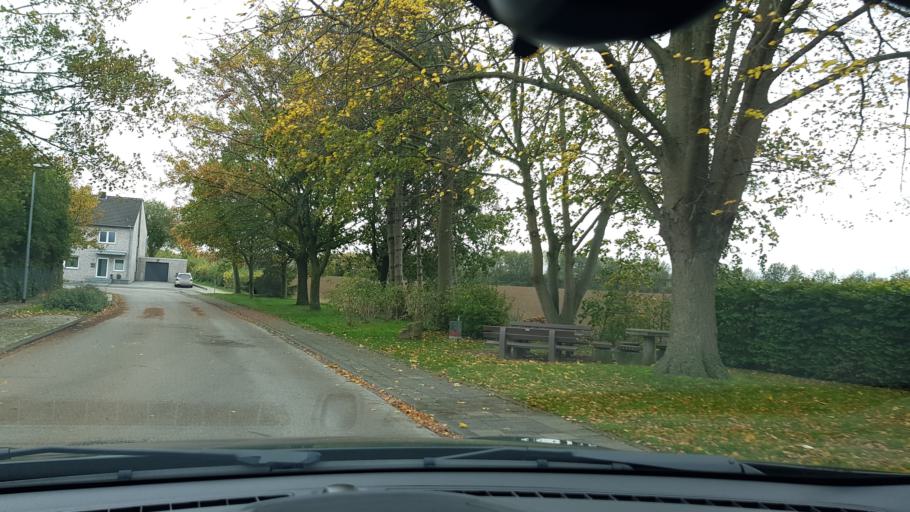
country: DE
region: North Rhine-Westphalia
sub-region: Regierungsbezirk Koln
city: Bedburg
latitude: 51.0011
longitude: 6.5415
